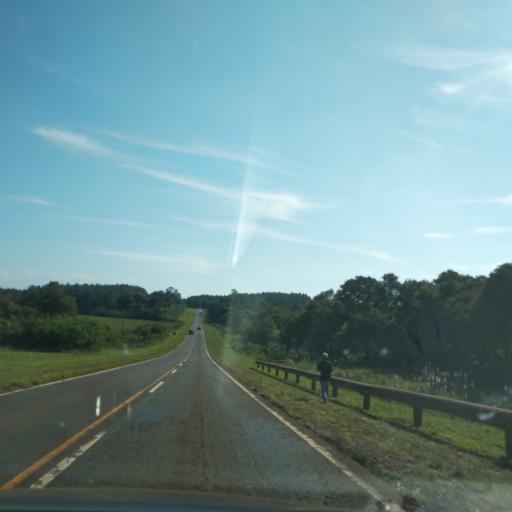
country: AR
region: Misiones
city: Santo Pipo
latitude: -27.1135
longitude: -55.3553
